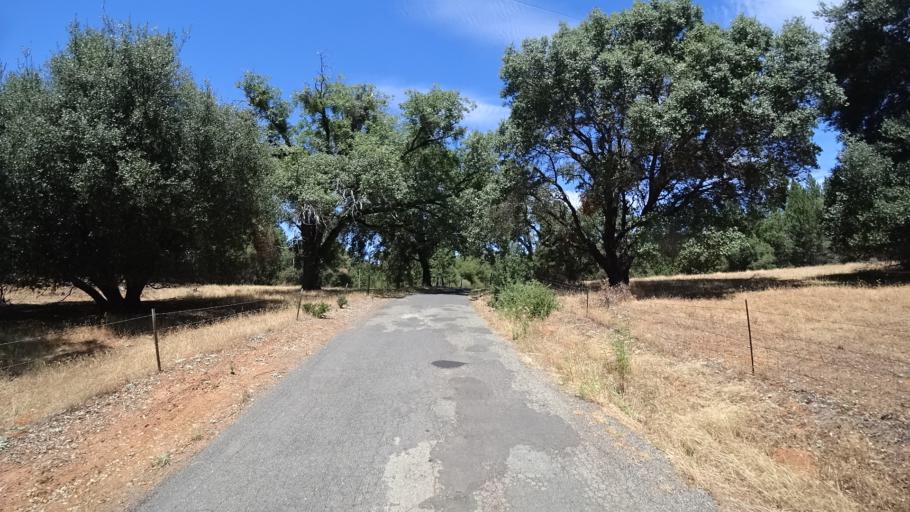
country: US
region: California
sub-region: Calaveras County
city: Forest Meadows
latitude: 38.2288
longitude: -120.4496
